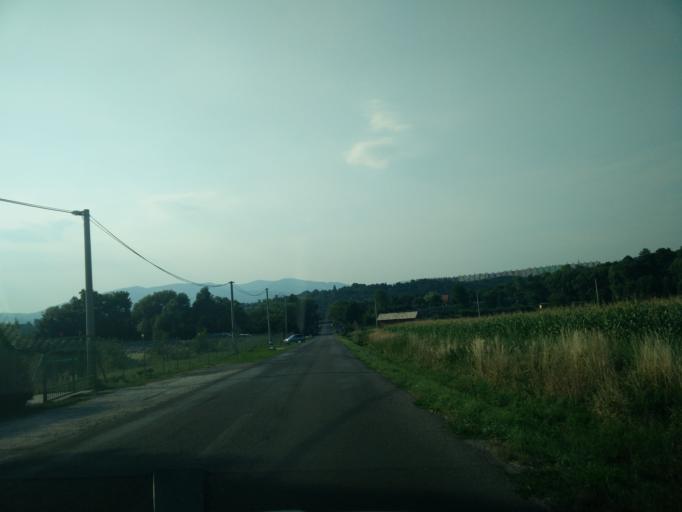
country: SK
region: Nitriansky
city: Prievidza
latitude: 48.7655
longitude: 18.6504
